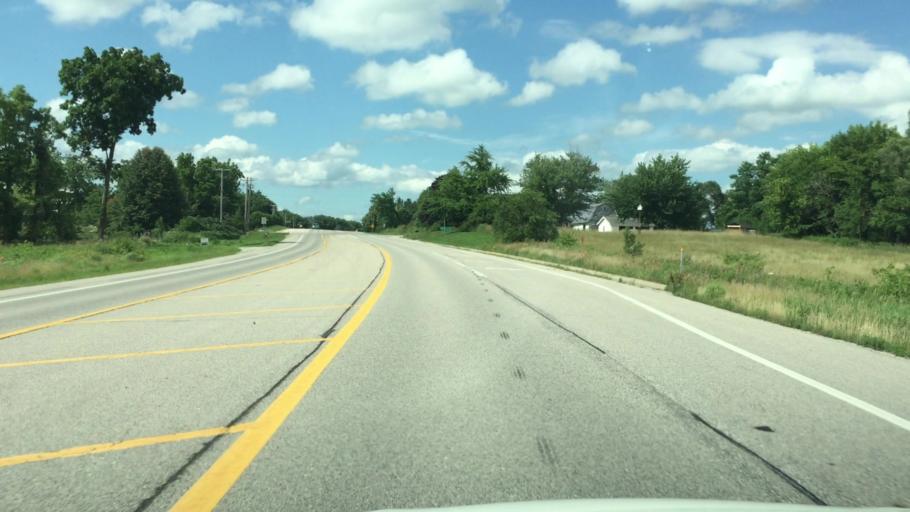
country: US
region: Iowa
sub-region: Johnson County
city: Solon
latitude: 41.7367
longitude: -91.4738
